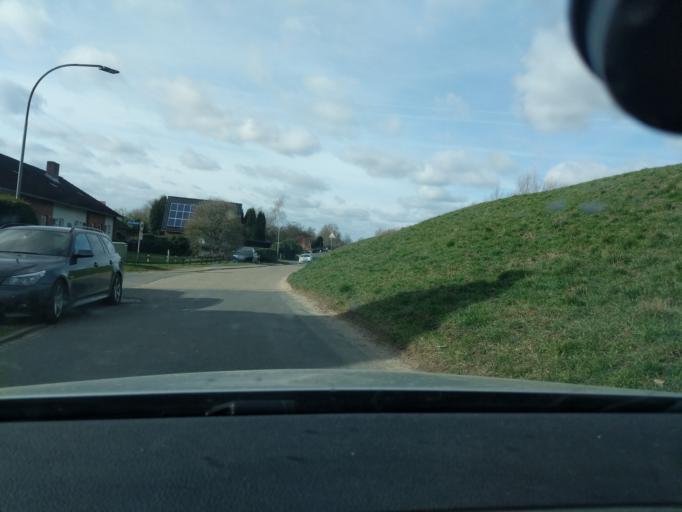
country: DE
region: Lower Saxony
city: Drochtersen
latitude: 53.7152
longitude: 9.3868
